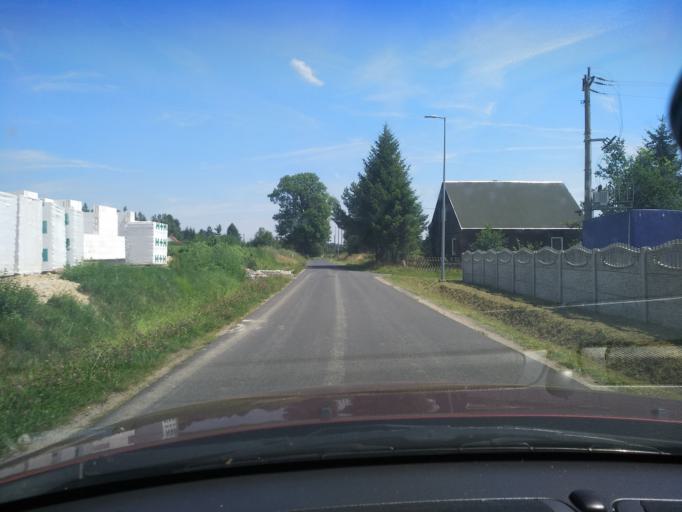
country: PL
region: Lower Silesian Voivodeship
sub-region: Powiat lwowecki
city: Mirsk
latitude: 50.9671
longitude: 15.3347
